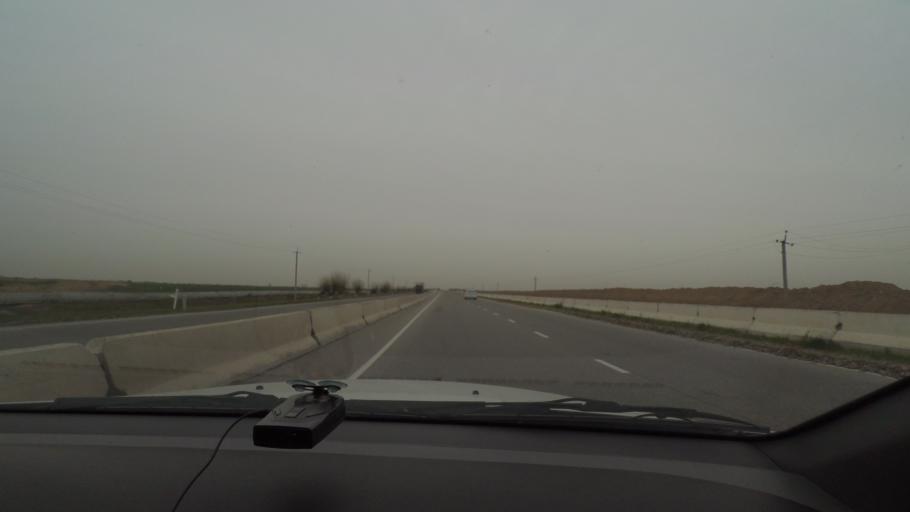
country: UZ
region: Jizzax
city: Gagarin
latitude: 40.4627
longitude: 68.2636
